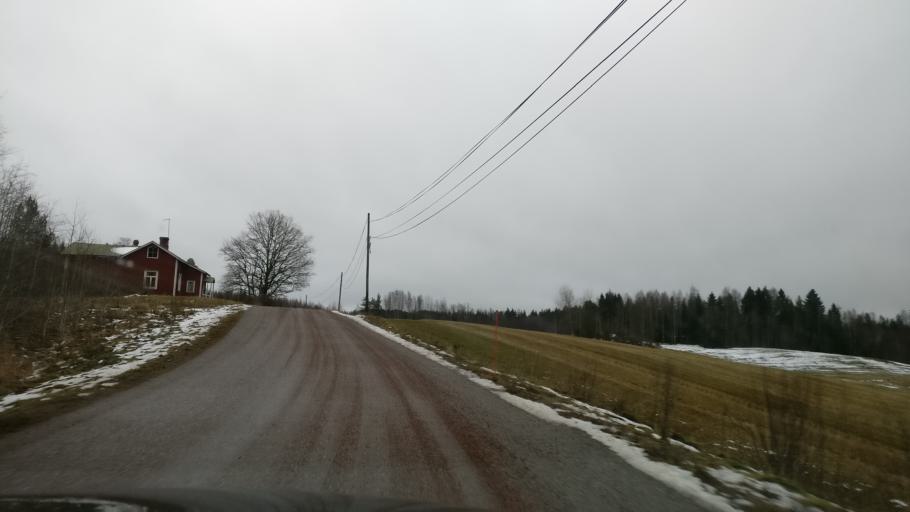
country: FI
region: Uusimaa
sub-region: Raaseporin
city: Karis
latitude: 60.0835
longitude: 23.7795
